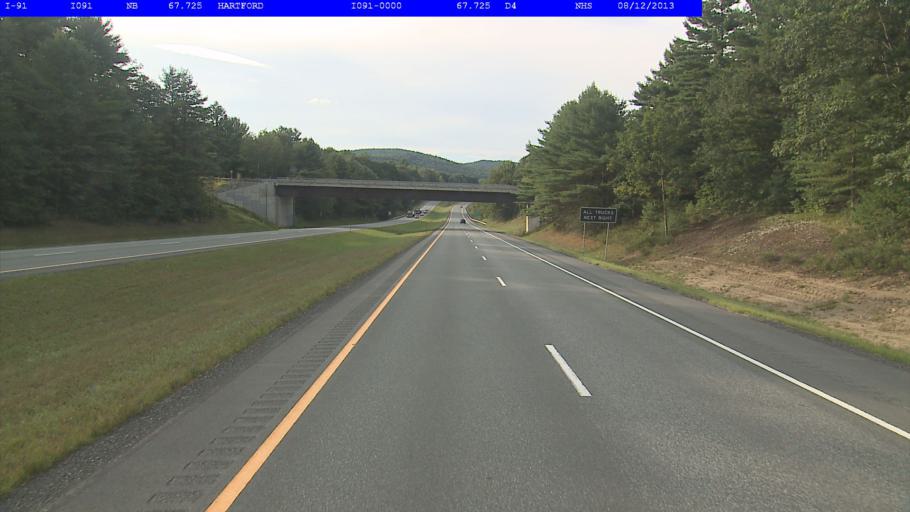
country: US
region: Vermont
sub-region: Windsor County
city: White River Junction
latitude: 43.6113
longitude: -72.3445
